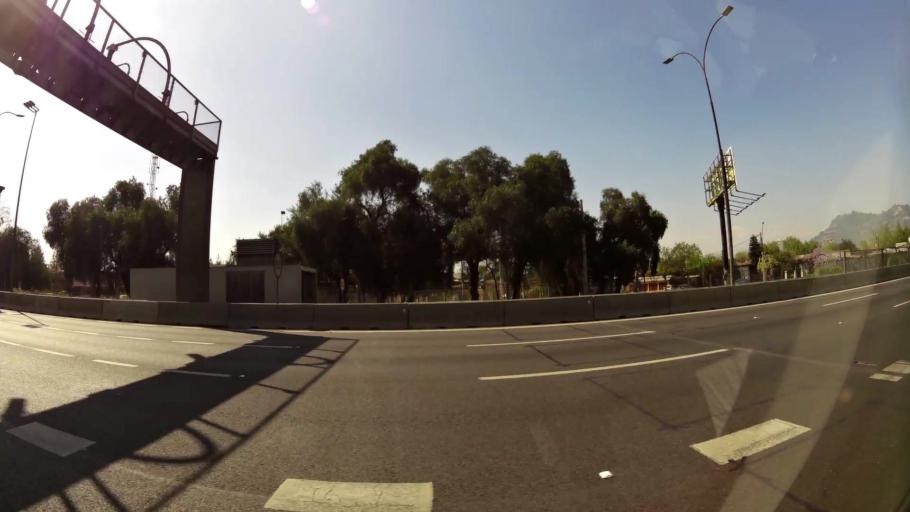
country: CL
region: Santiago Metropolitan
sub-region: Provincia de Santiago
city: Santiago
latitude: -33.4266
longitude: -70.6687
